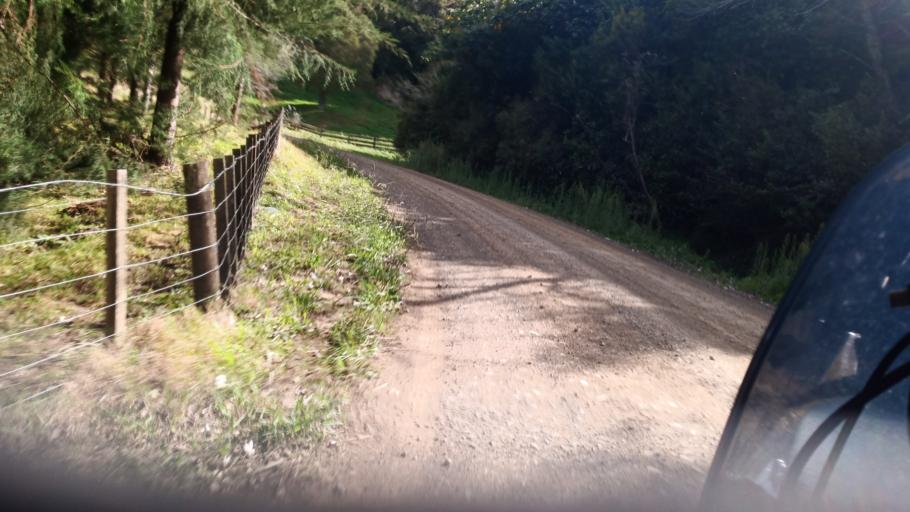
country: NZ
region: Gisborne
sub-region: Gisborne District
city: Gisborne
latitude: -38.4195
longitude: 177.7030
